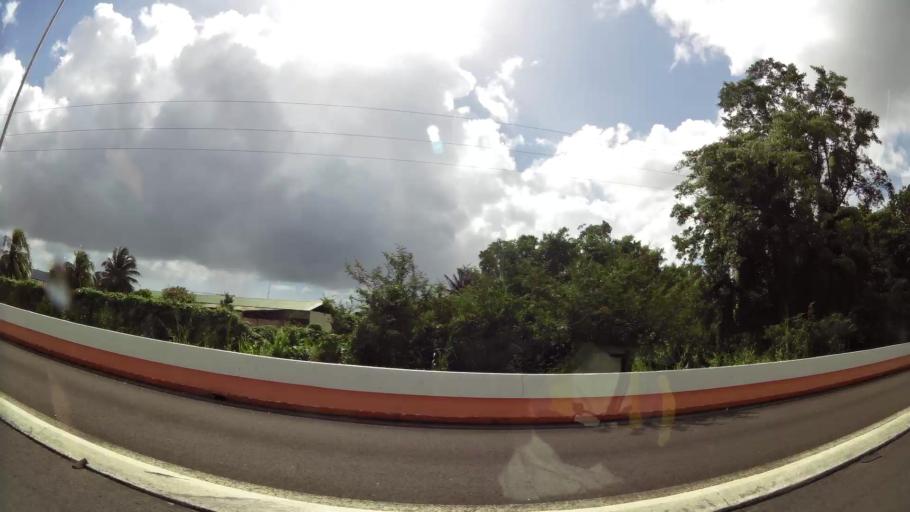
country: MQ
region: Martinique
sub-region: Martinique
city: Le Lamentin
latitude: 14.6115
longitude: -61.0077
